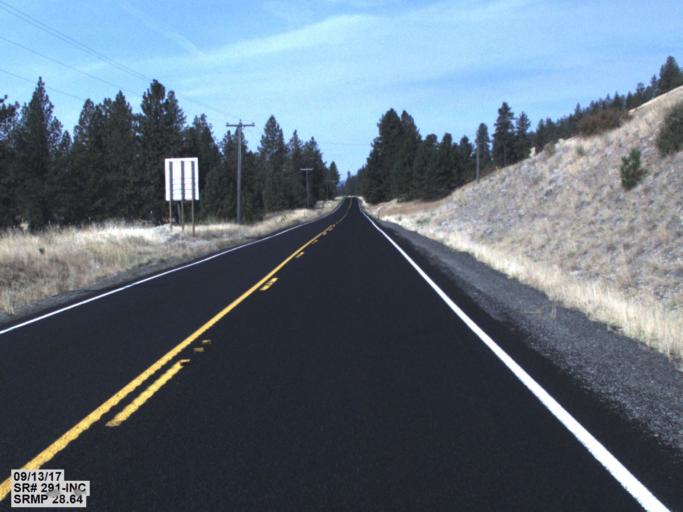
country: US
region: Washington
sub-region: Spokane County
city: Fairchild Air Force Base
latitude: 47.8389
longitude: -117.7662
